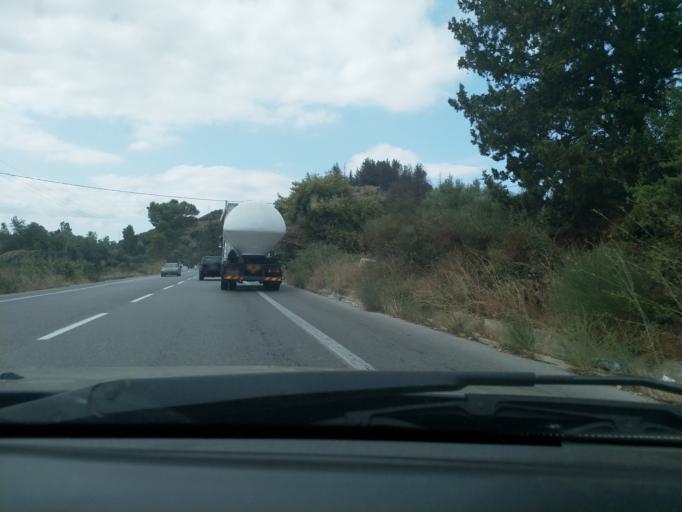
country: GR
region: Crete
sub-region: Nomos Chanias
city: Georgioupolis
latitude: 35.3768
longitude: 24.2074
